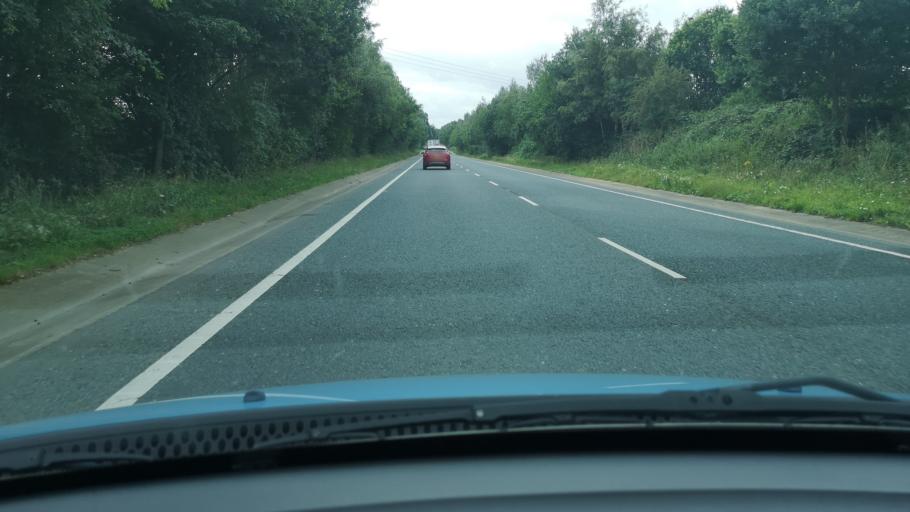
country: GB
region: England
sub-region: City and Borough of Wakefield
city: Hemsworth
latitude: 53.6030
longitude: -1.3550
